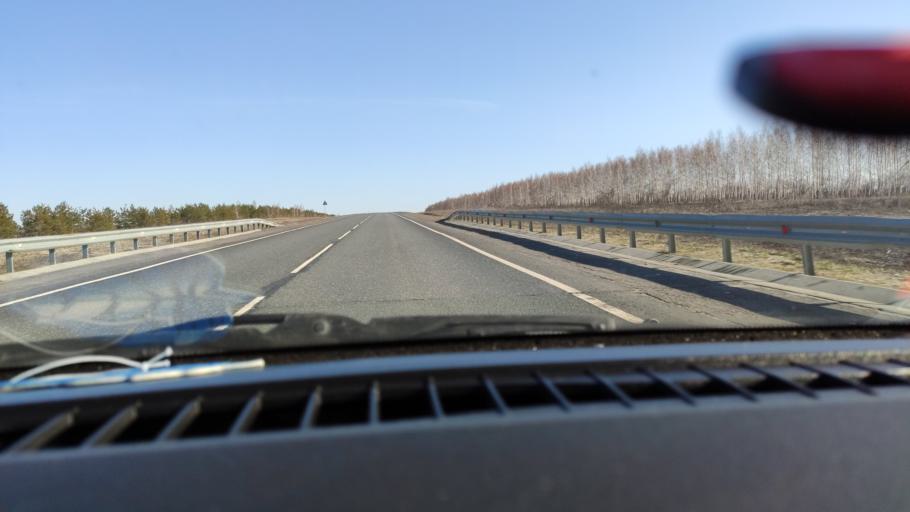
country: RU
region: Samara
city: Syzran'
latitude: 52.8891
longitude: 48.2944
